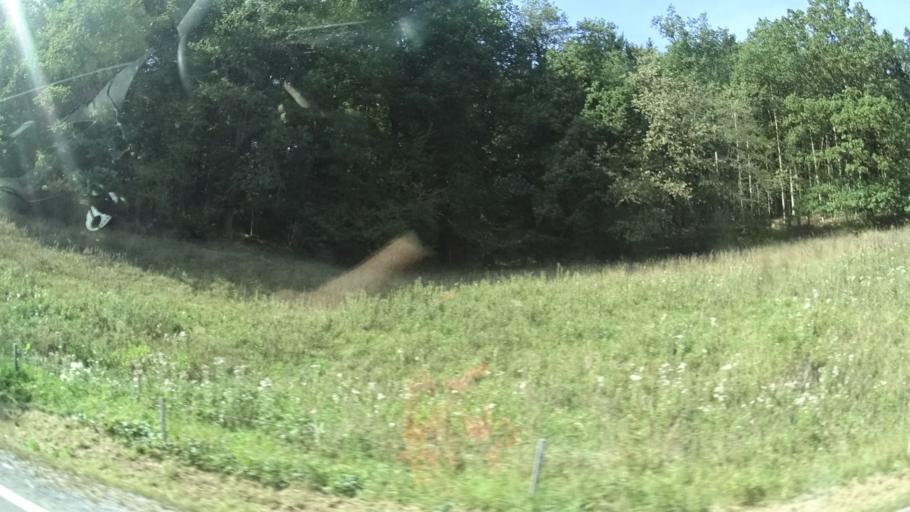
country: DE
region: Thuringia
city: Metzels
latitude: 50.6427
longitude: 10.4187
